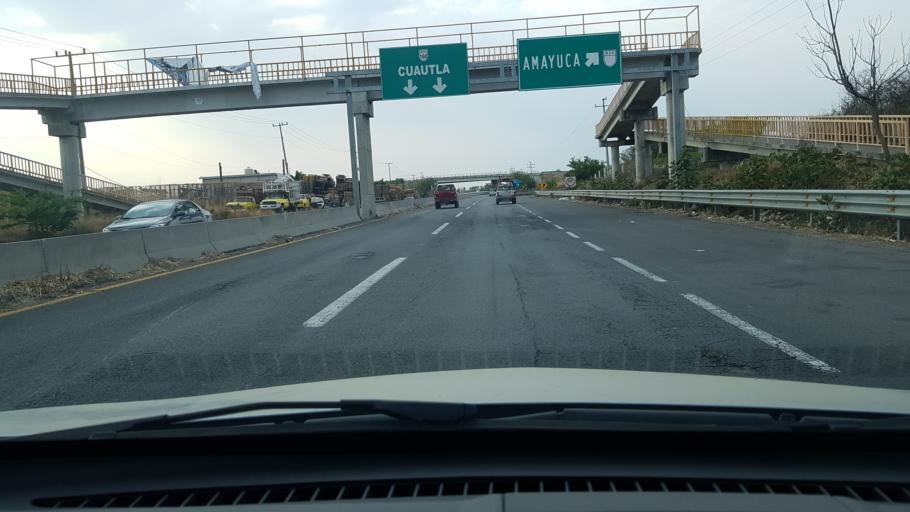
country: MX
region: Morelos
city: Amayuca
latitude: 18.7285
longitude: -98.8097
